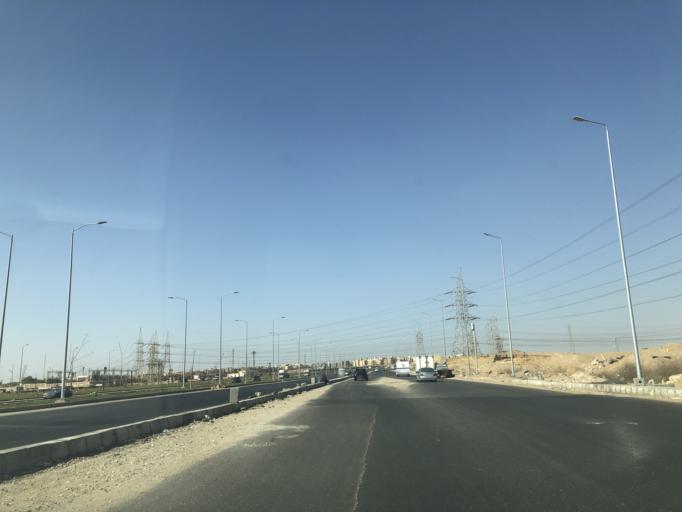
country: EG
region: Al Jizah
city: Madinat Sittah Uktubar
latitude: 29.9421
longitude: 30.9484
